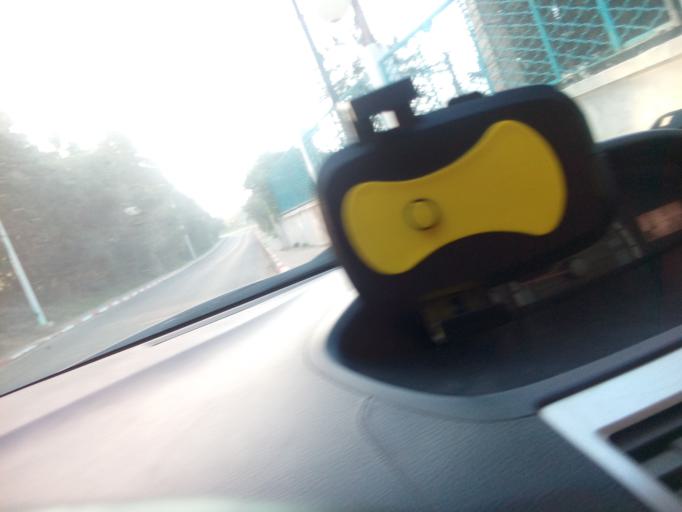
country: DZ
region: Oran
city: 'Ain el Turk
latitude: 35.7028
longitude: -0.8925
